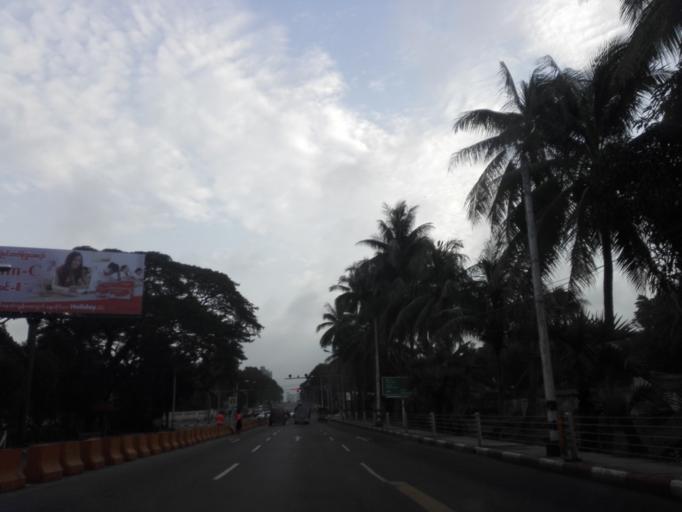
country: MM
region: Yangon
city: Yangon
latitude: 16.8522
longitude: 96.1406
